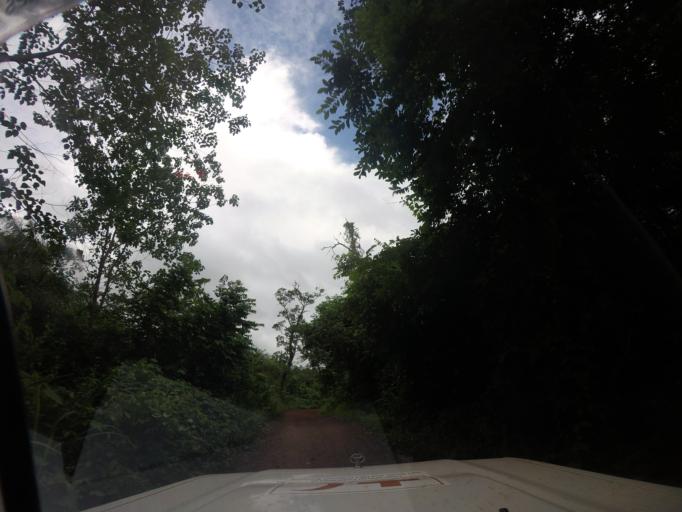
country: SL
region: Northern Province
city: Kamakwie
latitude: 9.6709
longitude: -12.2163
